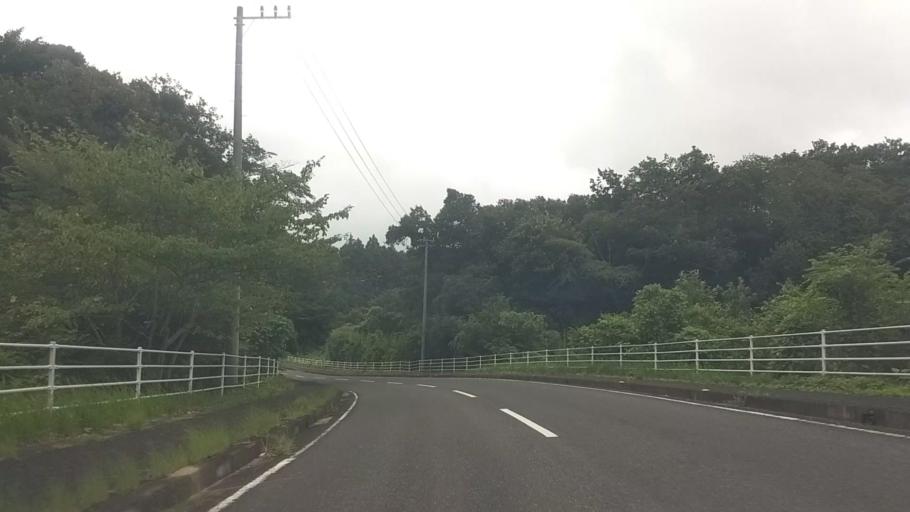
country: JP
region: Chiba
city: Kawaguchi
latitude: 35.2358
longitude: 140.0852
